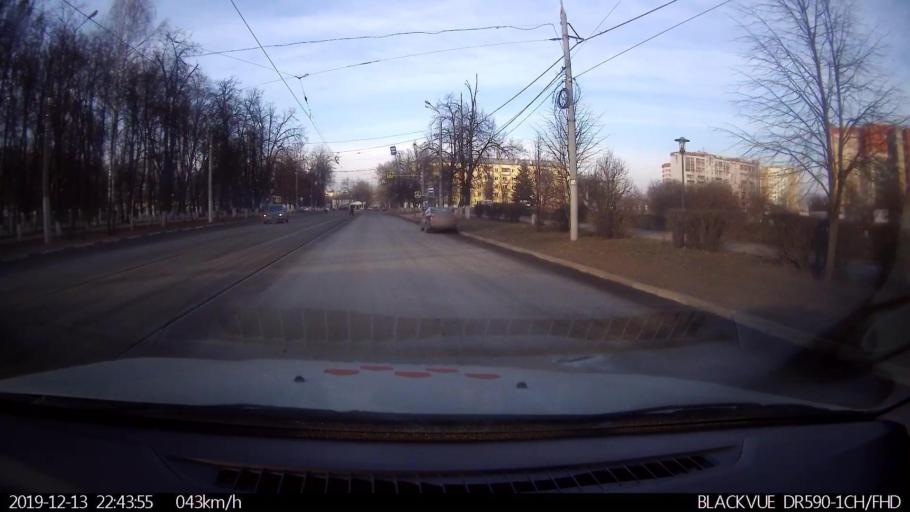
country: RU
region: Nizjnij Novgorod
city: Nizhniy Novgorod
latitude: 56.3123
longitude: 43.9373
